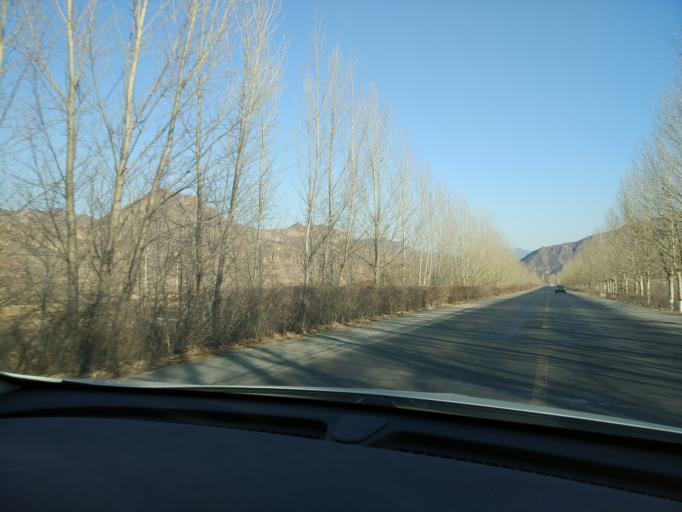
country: CN
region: Hebei
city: Chicheng
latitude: 40.7067
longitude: 115.7886
